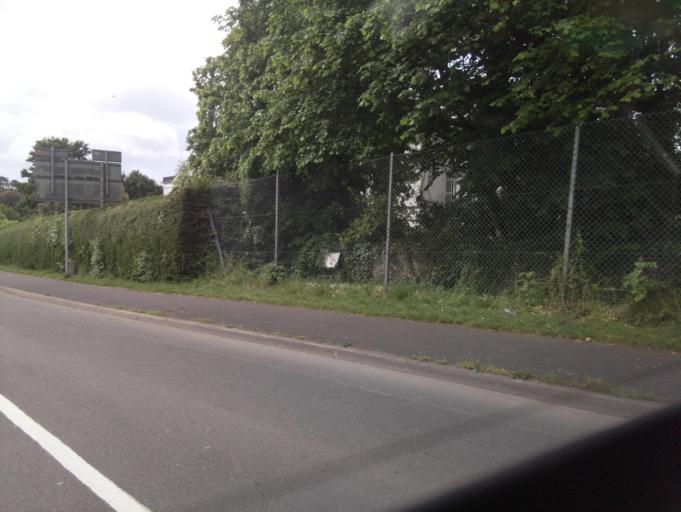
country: GB
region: England
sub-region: Devon
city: Newton Abbot
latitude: 50.5342
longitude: -3.6162
